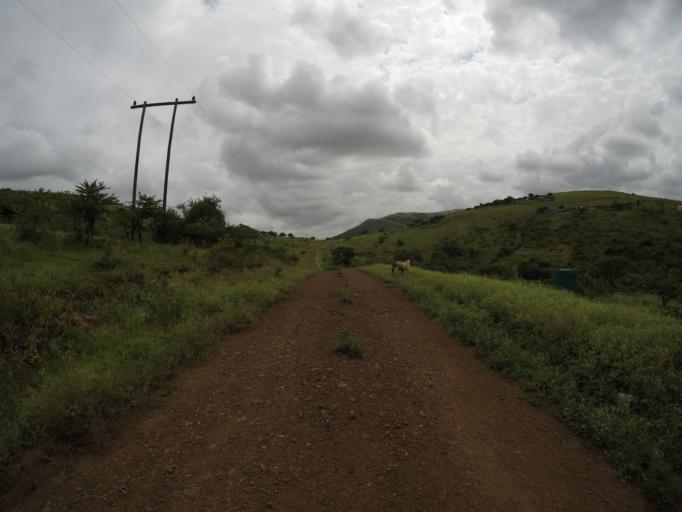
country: ZA
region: KwaZulu-Natal
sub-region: uThungulu District Municipality
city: Empangeni
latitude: -28.6214
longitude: 31.8912
